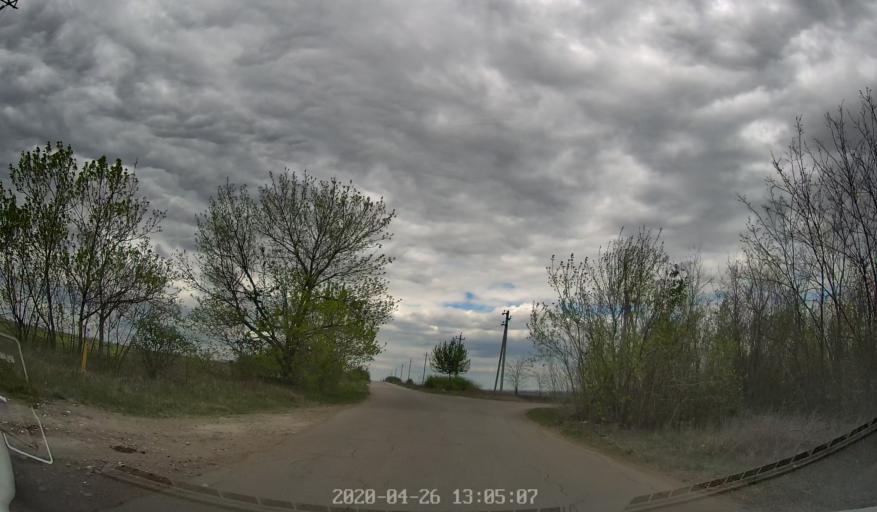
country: MD
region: Chisinau
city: Vadul lui Voda
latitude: 47.0738
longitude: 29.0658
